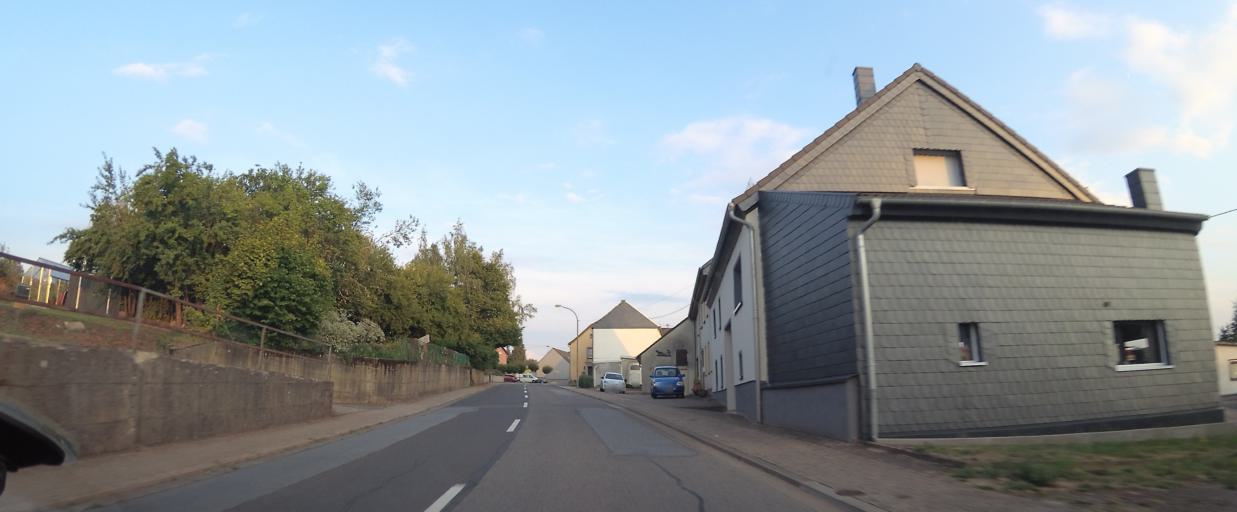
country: DE
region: Saarland
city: Wadern
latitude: 49.5753
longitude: 6.8977
